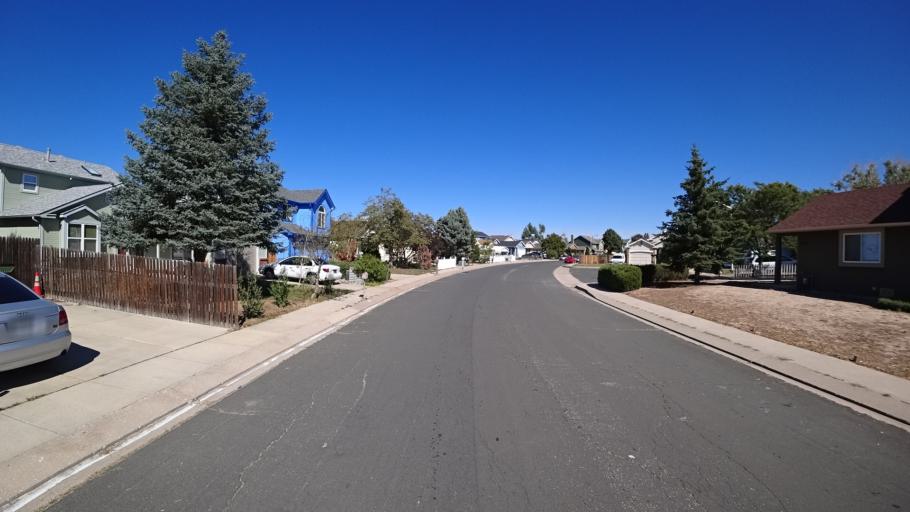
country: US
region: Colorado
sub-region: El Paso County
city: Stratmoor
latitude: 38.8115
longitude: -104.7422
